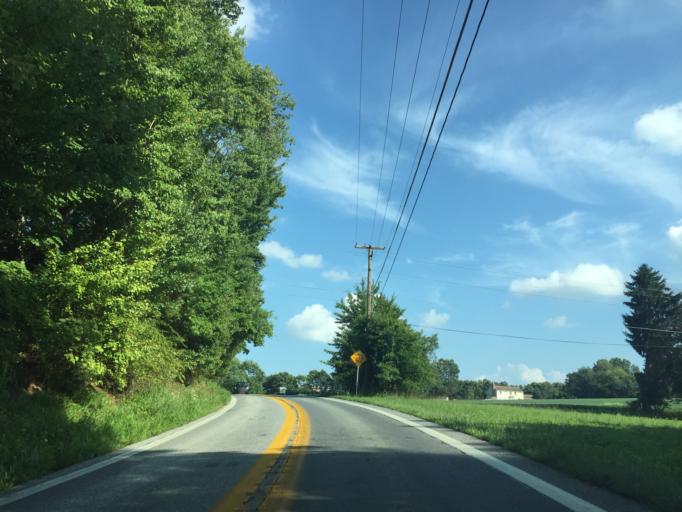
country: US
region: Maryland
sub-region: Carroll County
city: Hampstead
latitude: 39.6131
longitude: -76.7892
